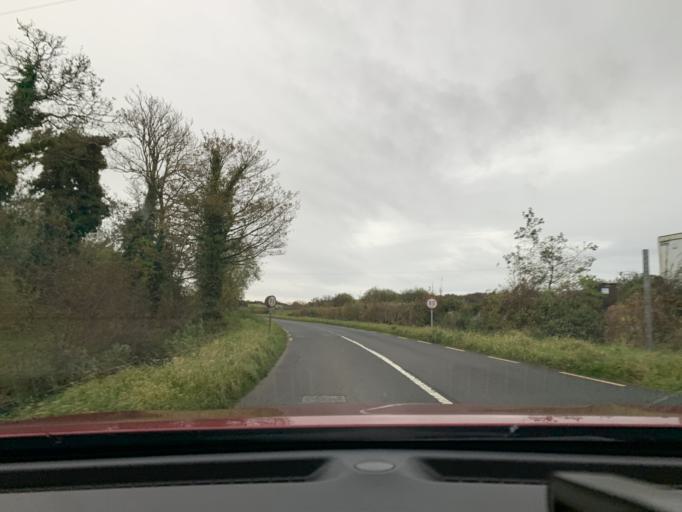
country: IE
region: Connaught
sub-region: Sligo
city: Ballymote
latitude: 54.0826
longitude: -8.5191
